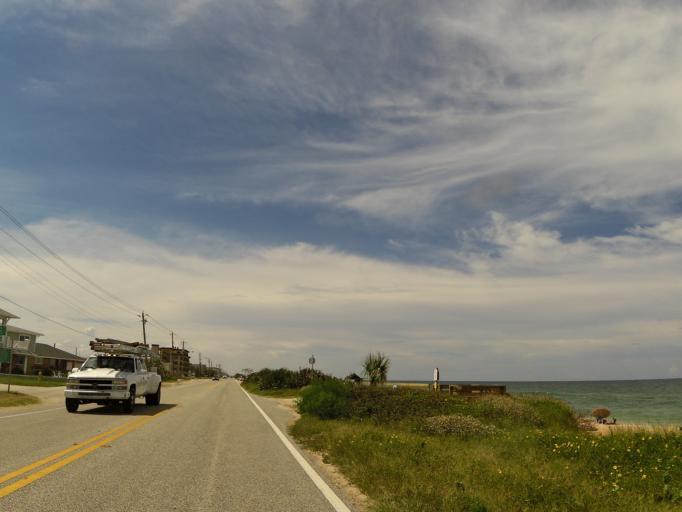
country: US
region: Florida
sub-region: Volusia County
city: Ormond-by-the-Sea
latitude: 29.3506
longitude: -81.0671
